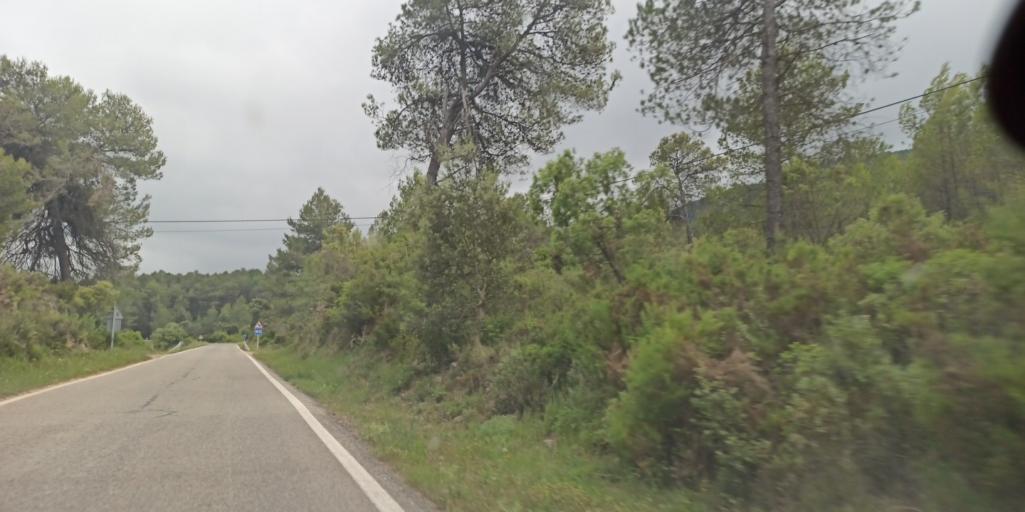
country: ES
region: Catalonia
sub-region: Provincia de Tarragona
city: la Bisbal del Penedes
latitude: 41.3633
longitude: 1.5024
